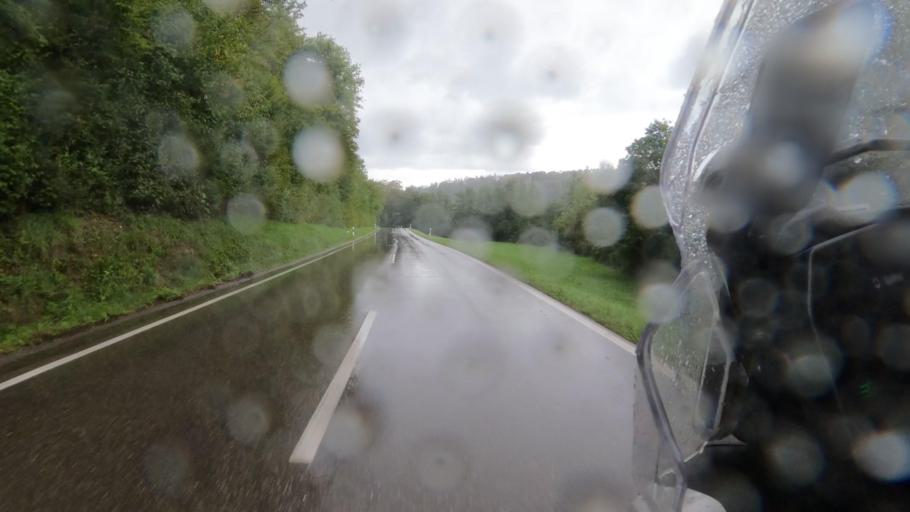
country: DE
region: Baden-Wuerttemberg
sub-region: Freiburg Region
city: Lottstetten
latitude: 47.6385
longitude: 8.5394
